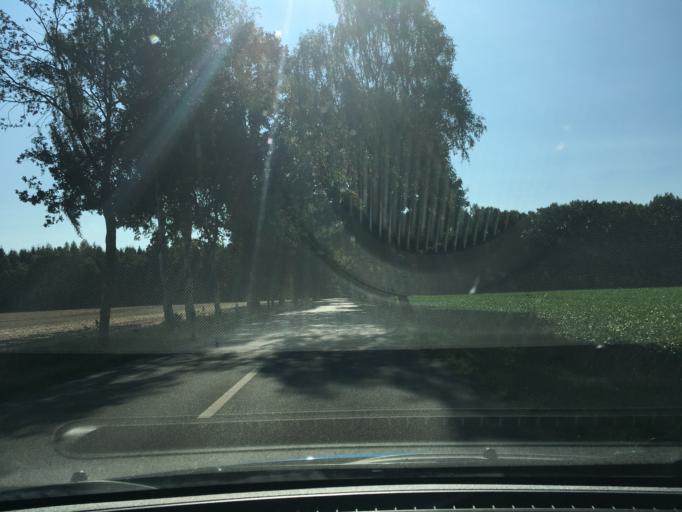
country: DE
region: Lower Saxony
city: Wriedel
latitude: 53.0496
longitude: 10.2545
